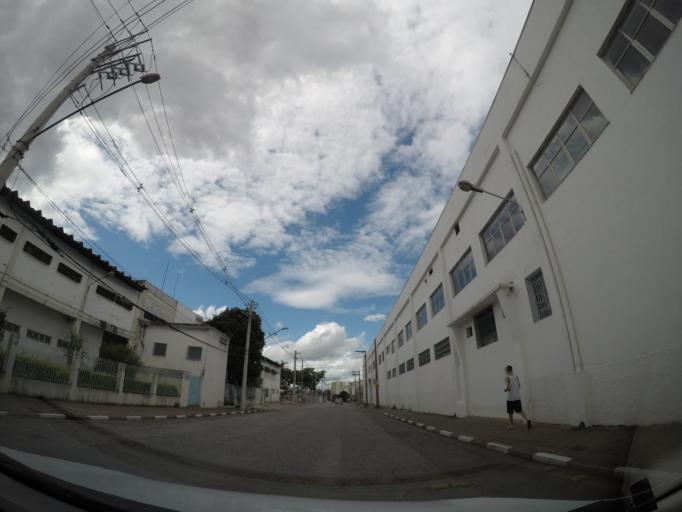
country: BR
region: Sao Paulo
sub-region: Guarulhos
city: Guarulhos
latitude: -23.4935
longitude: -46.5568
